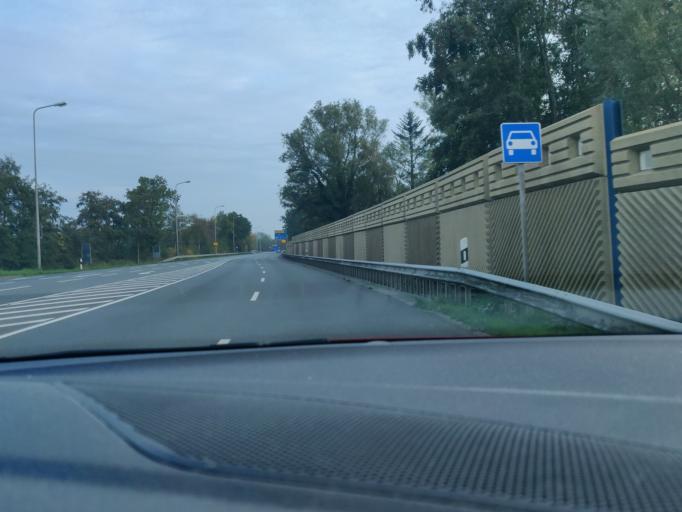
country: DE
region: Lower Saxony
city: Cuxhaven
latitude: 53.8449
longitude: 8.7300
